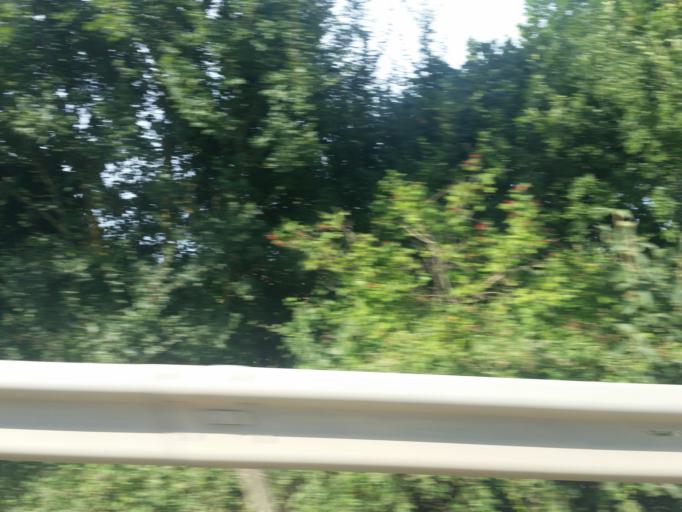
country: DE
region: Bavaria
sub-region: Lower Bavaria
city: Vilsbiburg
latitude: 48.4571
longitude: 12.3282
